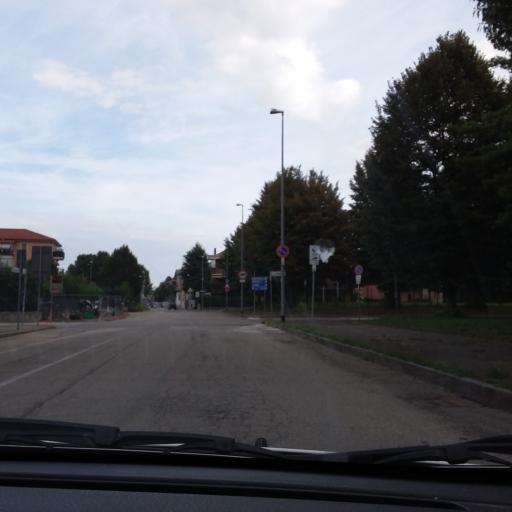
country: IT
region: Piedmont
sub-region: Provincia di Torino
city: Collegno
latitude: 45.0764
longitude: 7.5567
